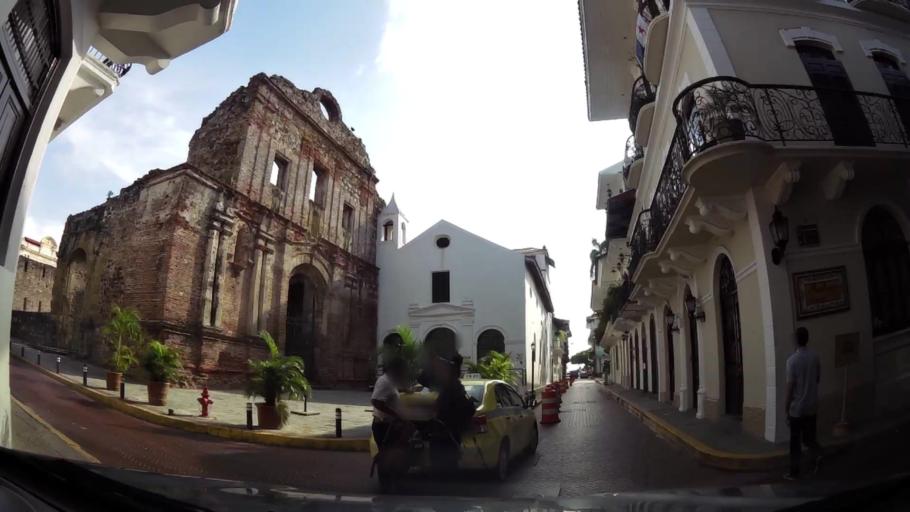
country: PA
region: Panama
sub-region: Distrito de Panama
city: Ancon
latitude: 8.9514
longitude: -79.5336
